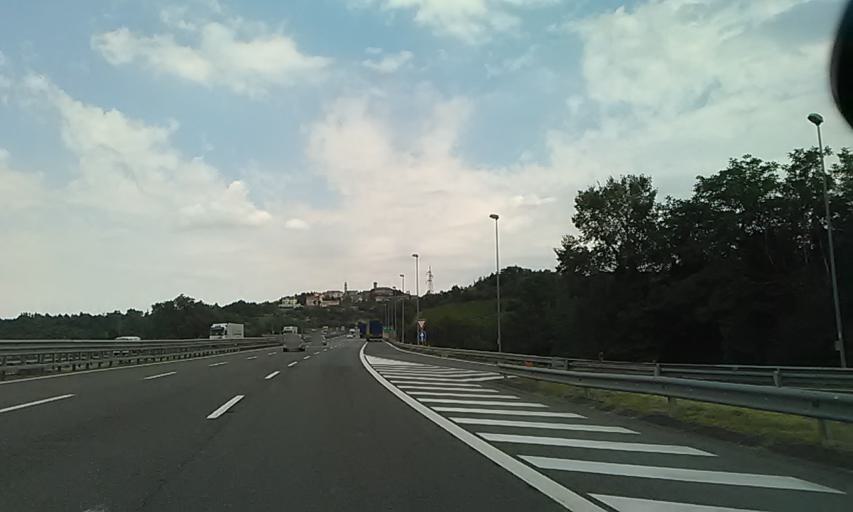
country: IT
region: Piedmont
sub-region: Provincia di Alessandria
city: Belforte Monferrato
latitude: 44.6284
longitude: 8.6591
